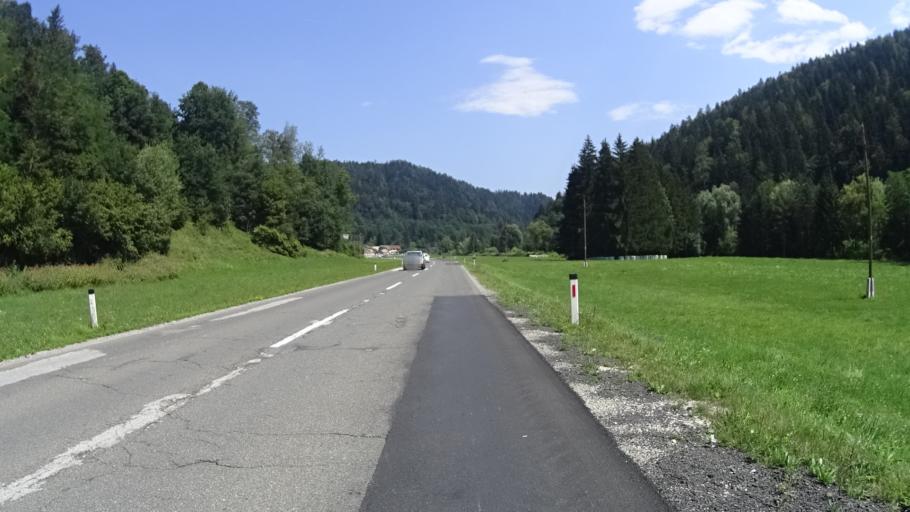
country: SI
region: Prevalje
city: Prevalje
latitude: 46.5471
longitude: 14.8855
